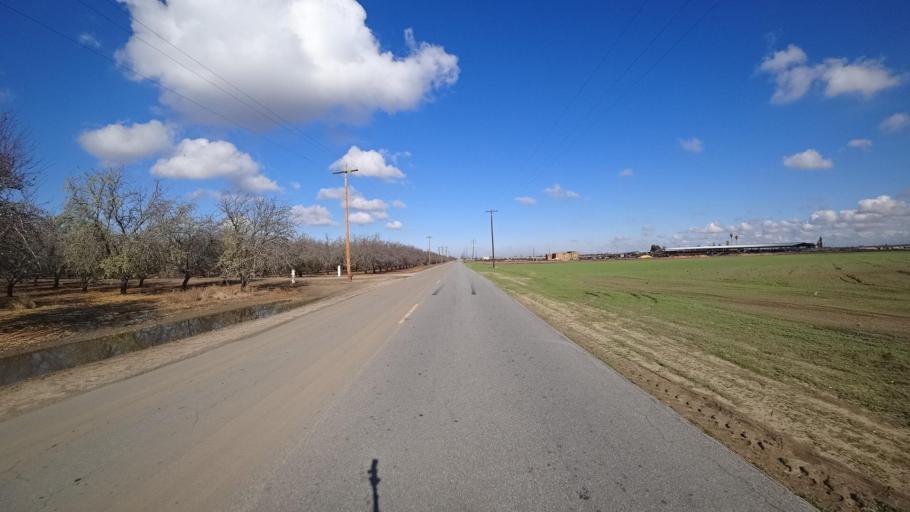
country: US
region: California
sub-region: Kern County
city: McFarland
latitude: 35.6558
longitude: -119.2409
